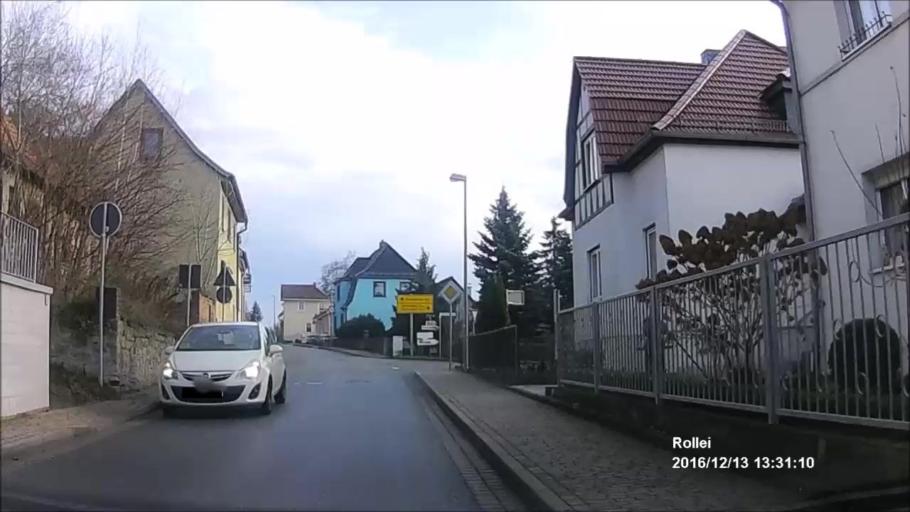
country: DE
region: Thuringia
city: Rittersdorf
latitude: 50.8575
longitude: 11.2500
